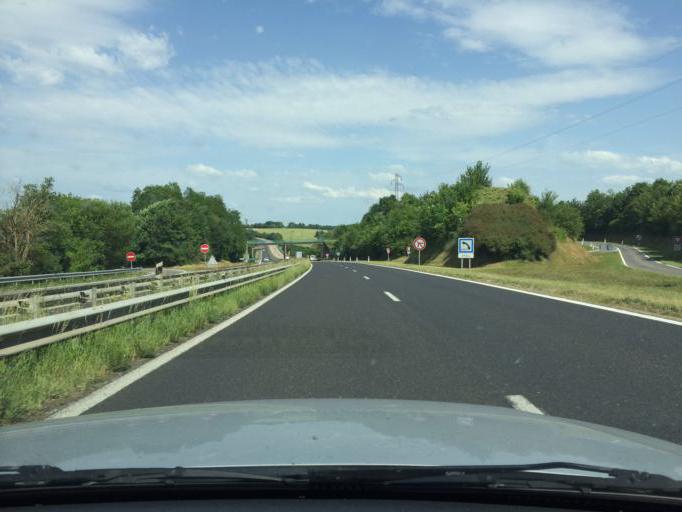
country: FR
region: Lorraine
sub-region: Departement de la Meuse
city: Longeville-en-Barrois
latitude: 48.6442
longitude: 5.1883
